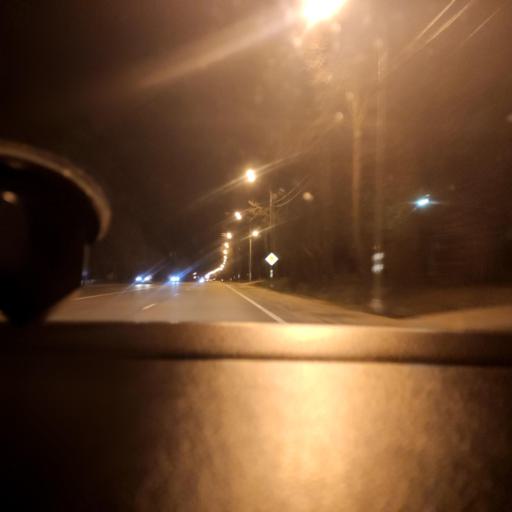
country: RU
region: Moskovskaya
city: Beloozerskiy
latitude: 55.3735
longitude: 38.3824
